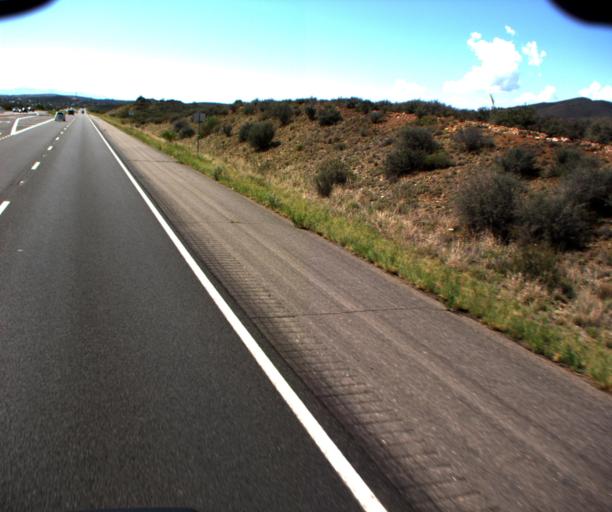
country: US
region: Arizona
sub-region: Yavapai County
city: Mayer
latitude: 34.4205
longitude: -112.2504
